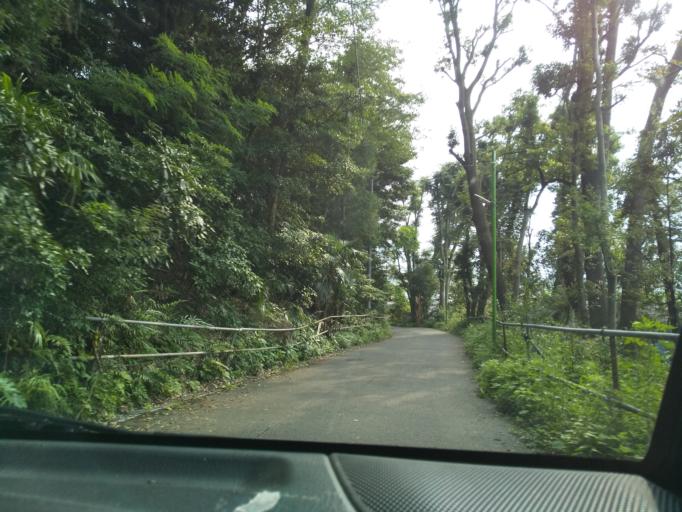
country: JP
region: Kanagawa
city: Zama
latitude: 35.4734
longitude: 139.3969
